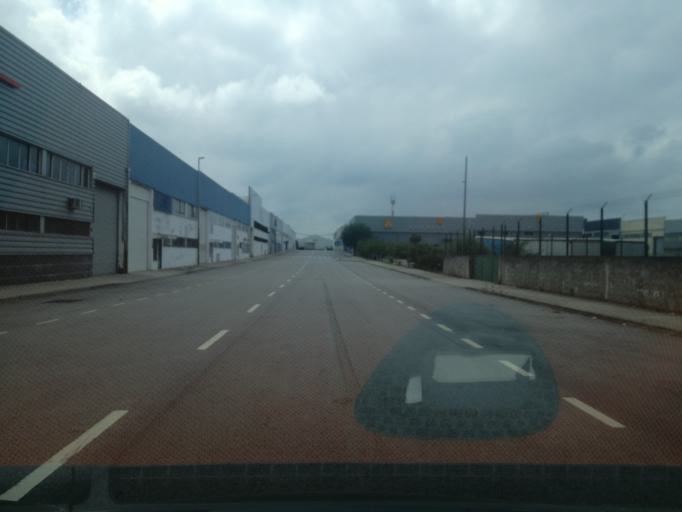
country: PT
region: Porto
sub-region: Maia
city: Anta
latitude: 41.2556
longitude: -8.6340
